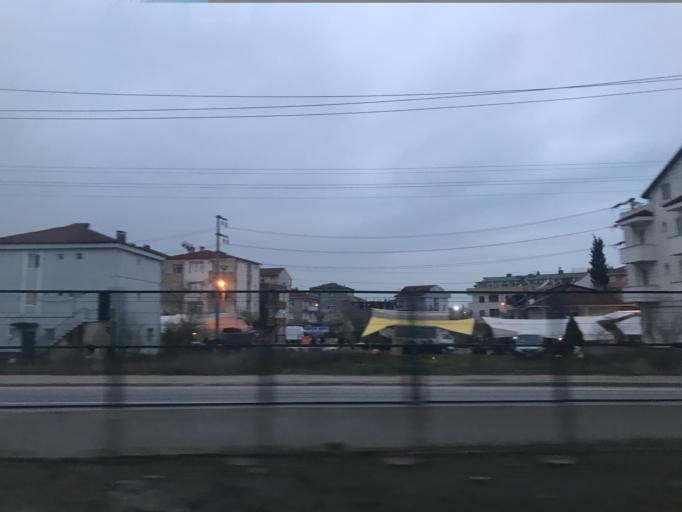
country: TR
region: Kocaeli
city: Darica
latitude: 40.7899
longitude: 29.3938
